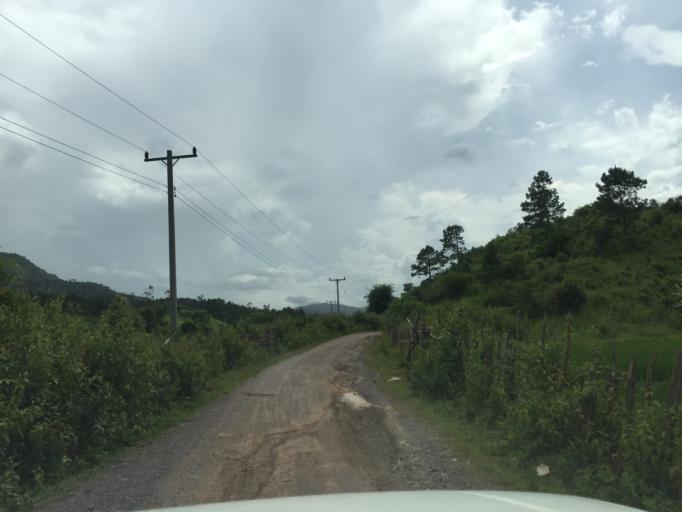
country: LA
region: Xiangkhoang
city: Muang Phonsavan
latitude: 19.3413
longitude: 103.5486
